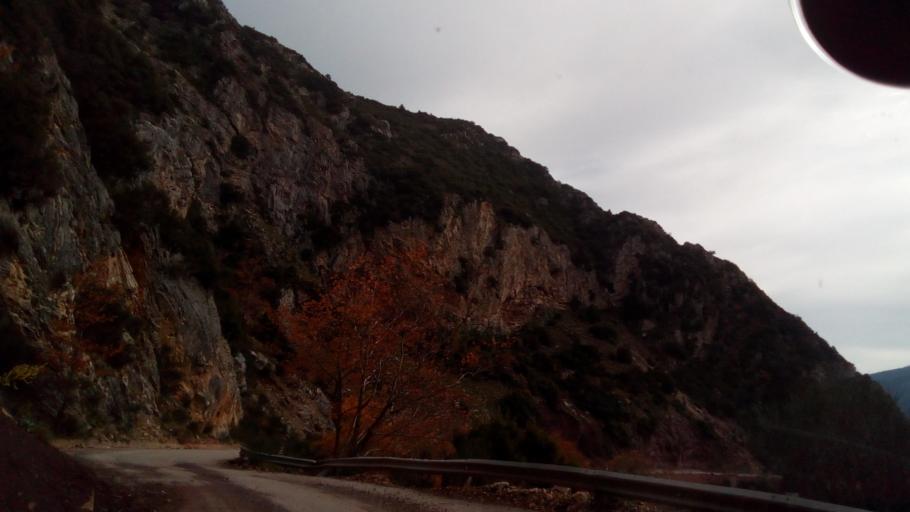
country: GR
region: West Greece
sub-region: Nomos Aitolias kai Akarnanias
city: Thermo
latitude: 38.6764
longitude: 21.8851
